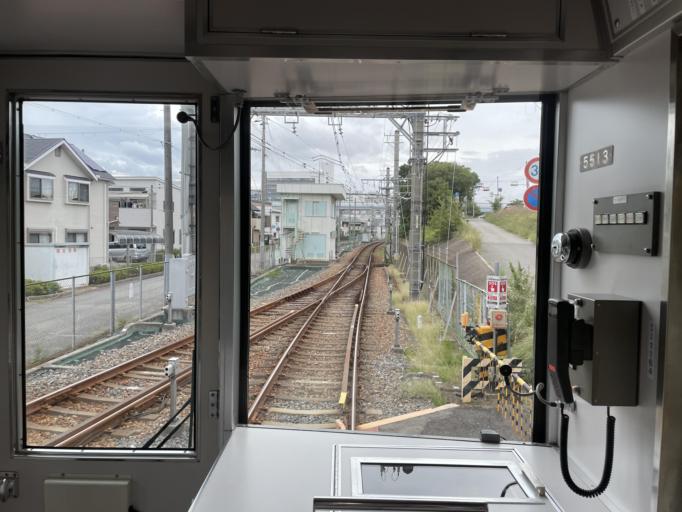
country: JP
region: Hyogo
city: Amagasaki
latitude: 34.7132
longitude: 135.3793
